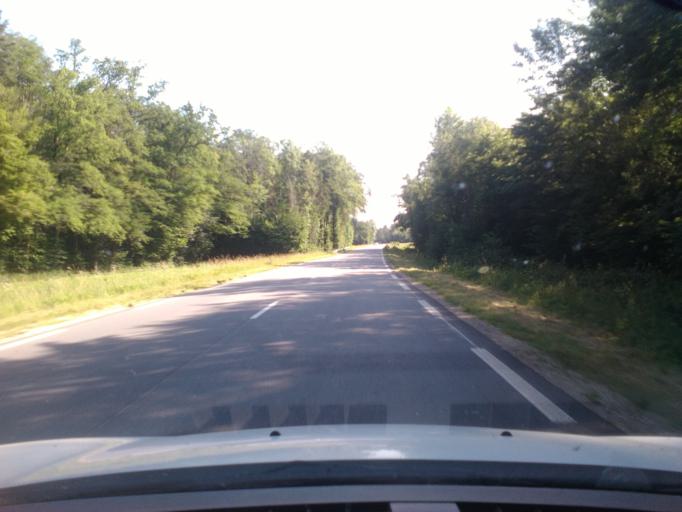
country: FR
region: Lorraine
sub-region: Departement des Vosges
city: Aydoilles
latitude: 48.2294
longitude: 6.5924
